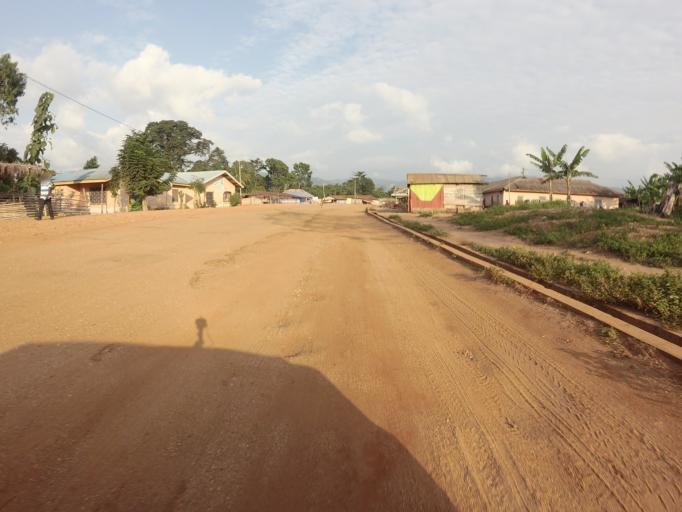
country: GH
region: Volta
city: Kpandu
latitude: 6.9639
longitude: 0.4587
